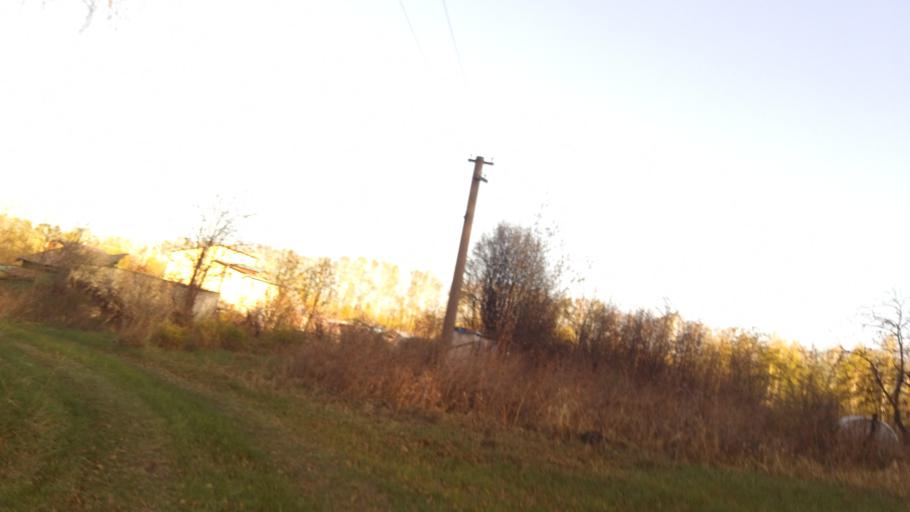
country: RU
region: Chelyabinsk
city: Timiryazevskiy
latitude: 54.9915
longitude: 60.8589
